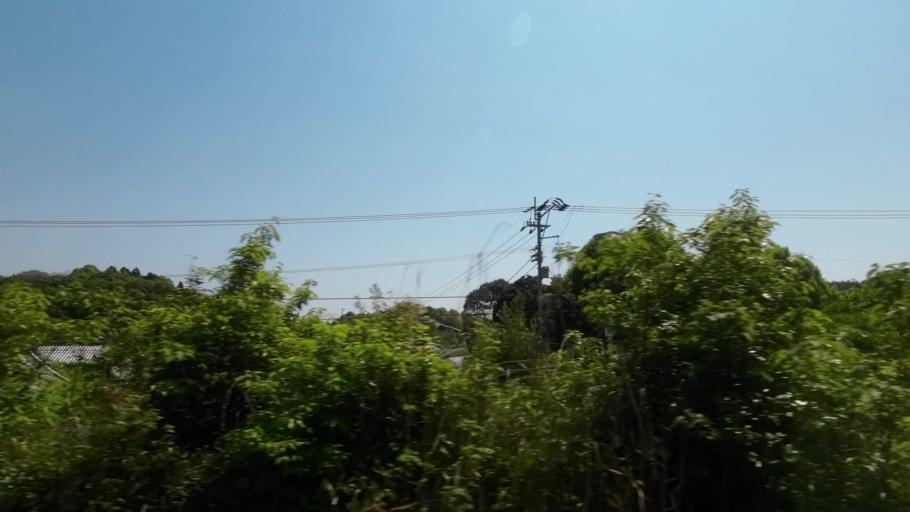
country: JP
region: Ehime
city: Saijo
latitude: 33.9895
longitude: 133.0522
